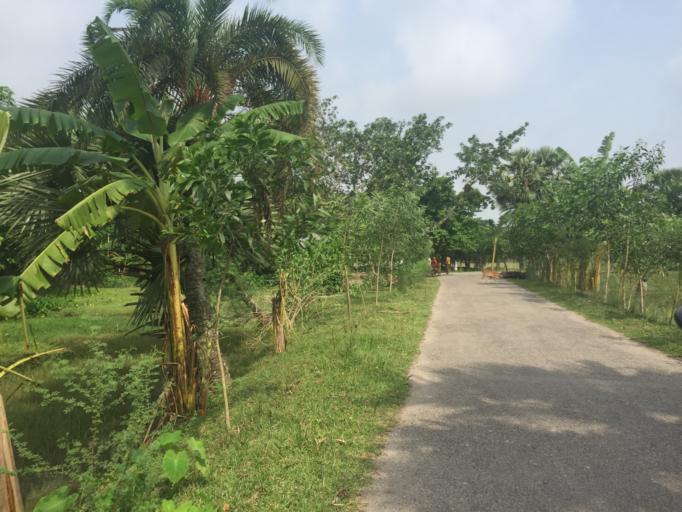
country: BD
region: Barisal
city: Mathba
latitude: 22.2556
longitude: 89.9112
